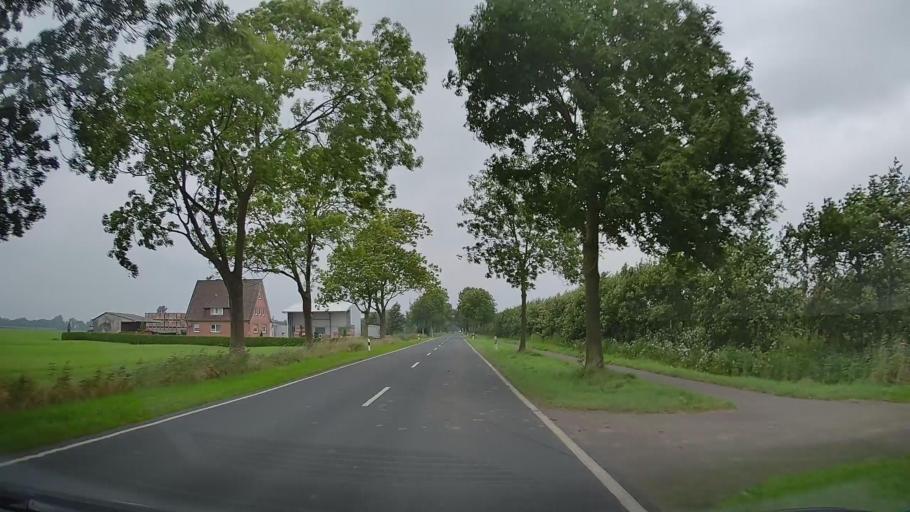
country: DE
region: Lower Saxony
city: Balje
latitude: 53.8170
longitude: 9.1311
